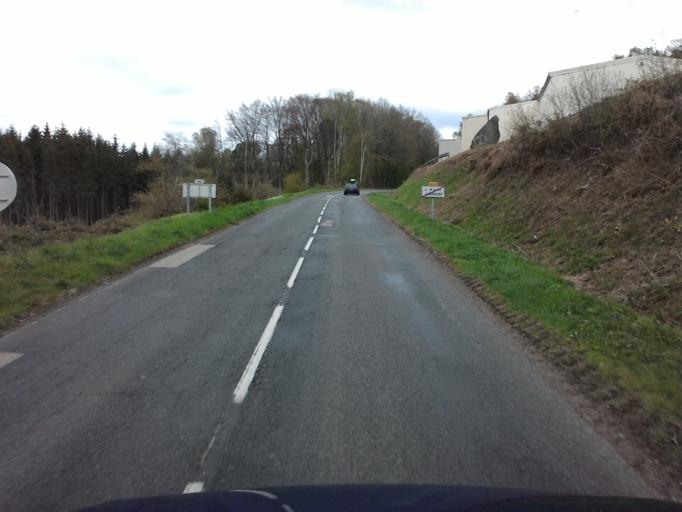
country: FR
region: Bourgogne
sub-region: Departement de la Cote-d'Or
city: Saulieu
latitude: 47.3160
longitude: 4.0401
